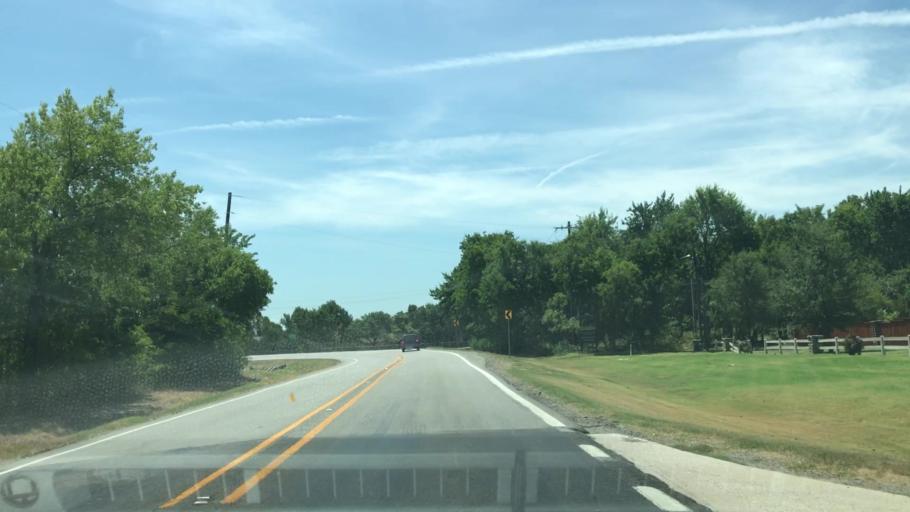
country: US
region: Texas
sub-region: Collin County
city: Fairview
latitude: 33.1211
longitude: -96.6093
